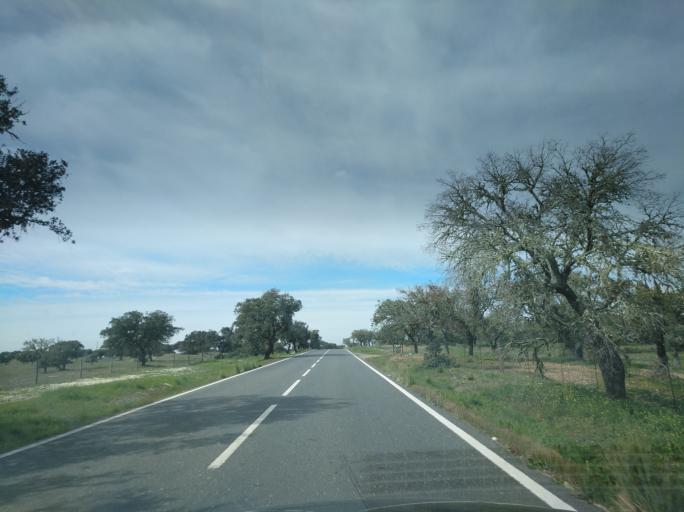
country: PT
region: Beja
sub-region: Mertola
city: Mertola
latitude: 37.7476
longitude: -7.7989
